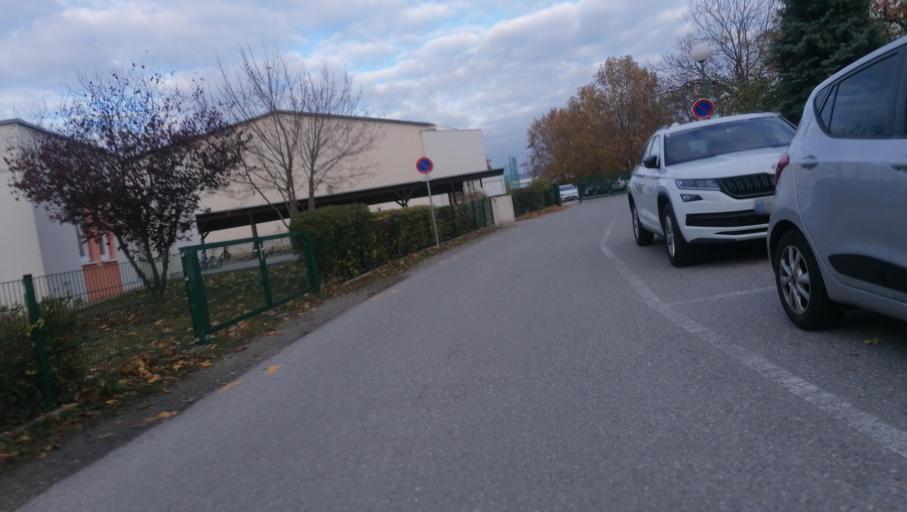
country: AT
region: Lower Austria
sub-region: Politischer Bezirk Baden
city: Oberwaltersdorf
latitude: 47.9783
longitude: 16.3212
